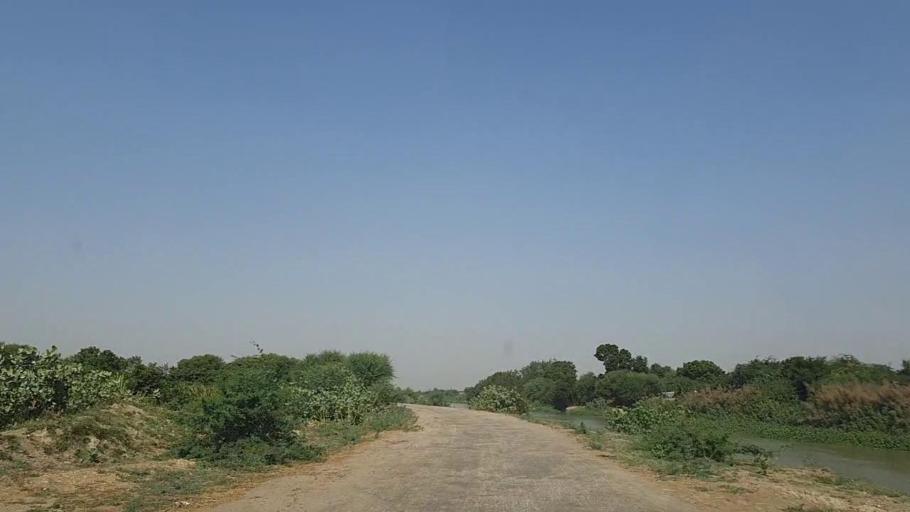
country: PK
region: Sindh
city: Daro Mehar
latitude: 24.7218
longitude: 68.1570
